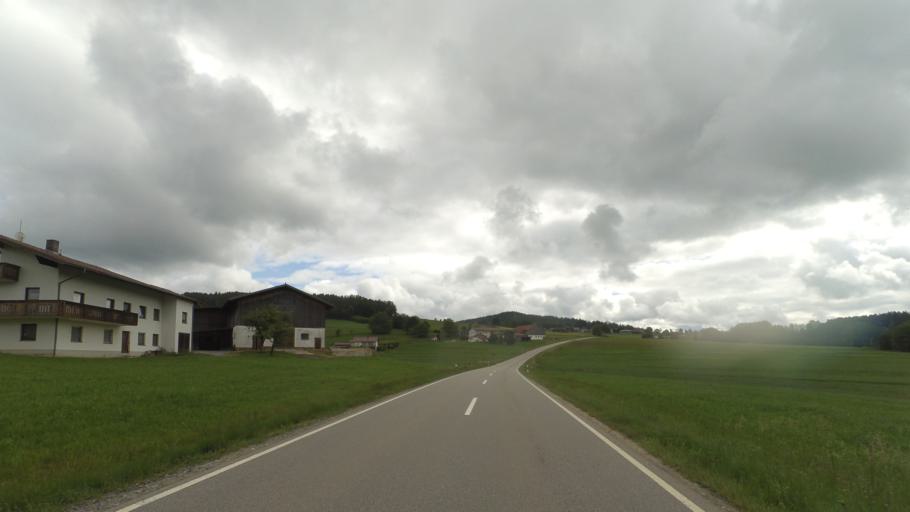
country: DE
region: Bavaria
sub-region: Lower Bavaria
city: Prackenbach
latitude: 49.0995
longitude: 12.7964
